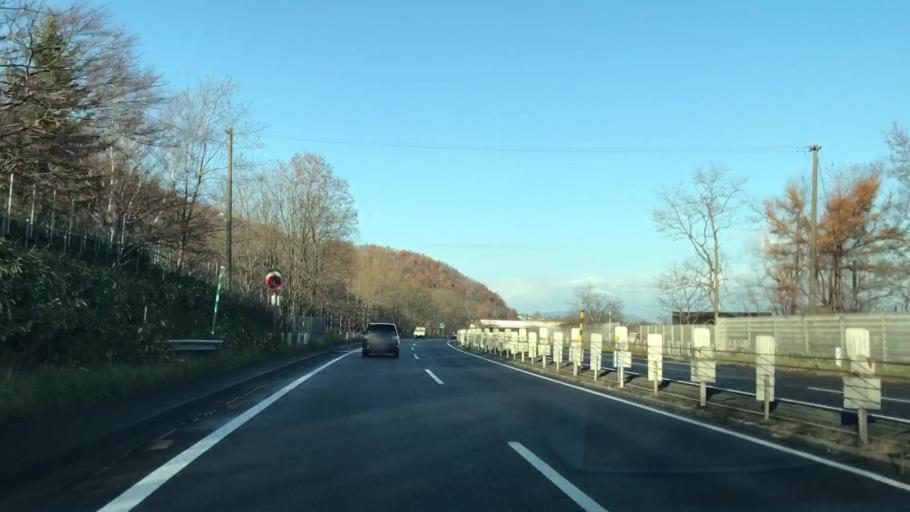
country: JP
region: Hokkaido
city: Sapporo
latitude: 43.1191
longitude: 141.2231
